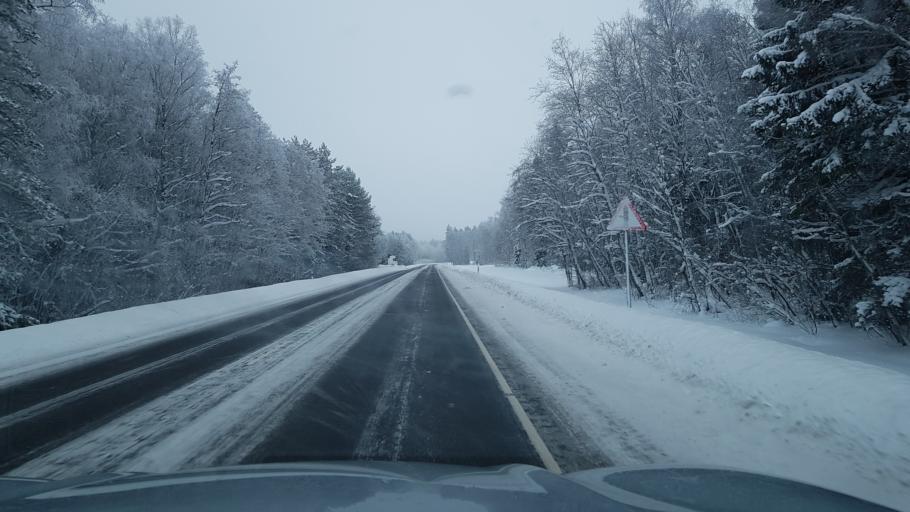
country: EE
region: Ida-Virumaa
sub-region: Johvi vald
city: Johvi
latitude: 59.2979
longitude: 27.3970
